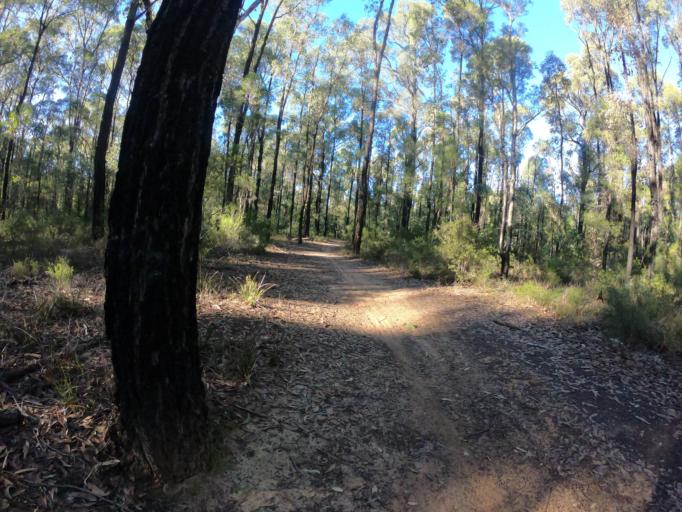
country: AU
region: New South Wales
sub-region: Hawkesbury
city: South Windsor
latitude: -33.6440
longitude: 150.7965
